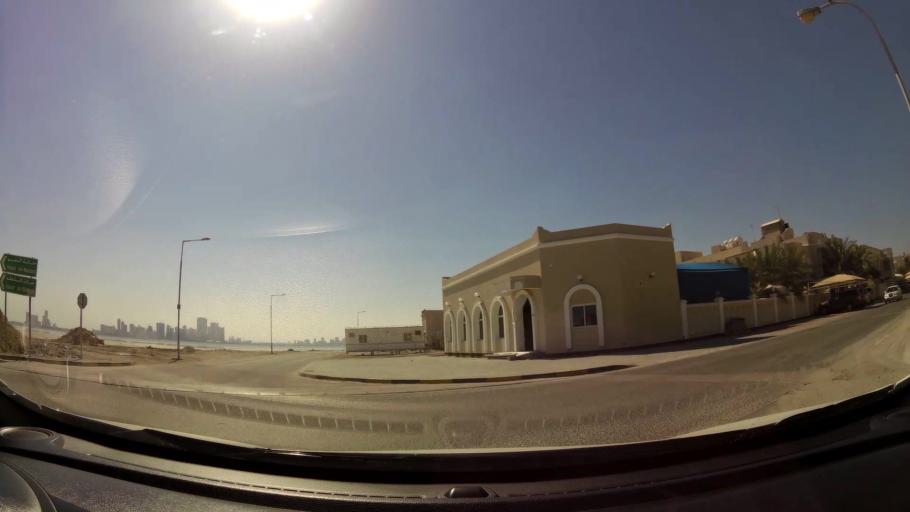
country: BH
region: Muharraq
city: Al Hadd
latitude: 26.2440
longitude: 50.6336
